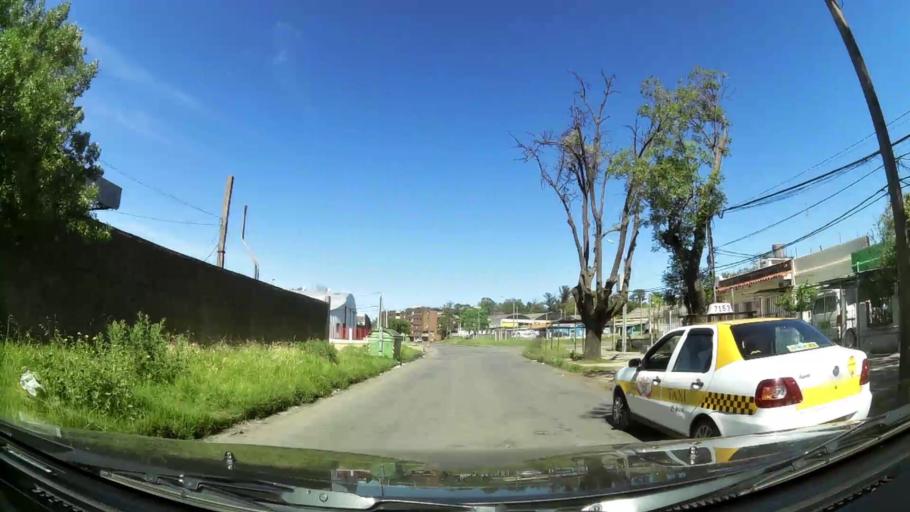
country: UY
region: Montevideo
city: Montevideo
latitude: -34.8697
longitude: -56.1284
